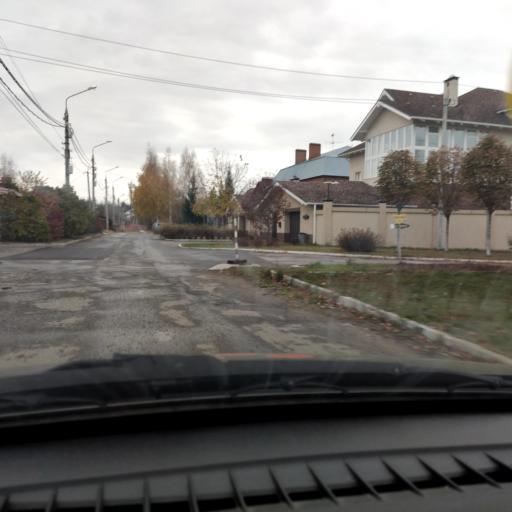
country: RU
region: Samara
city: Tol'yatti
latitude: 53.5430
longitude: 49.3733
